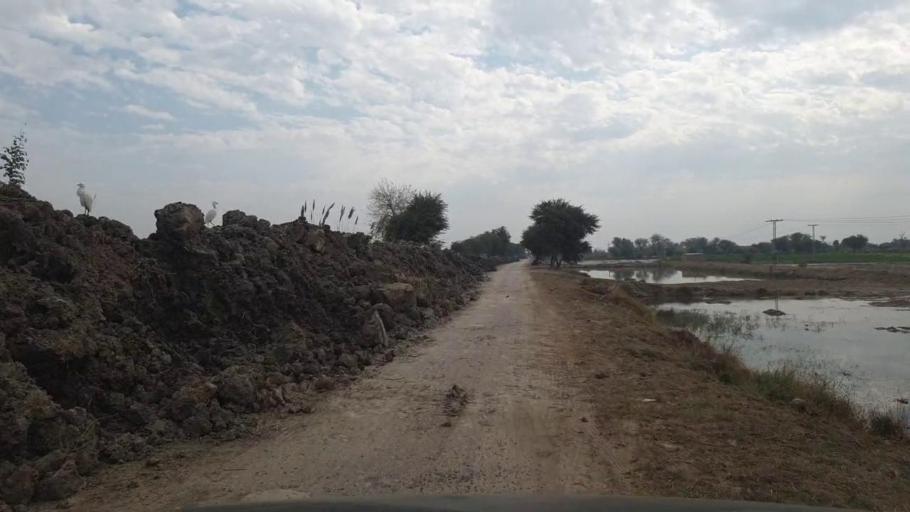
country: PK
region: Sindh
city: Sakrand
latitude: 26.0260
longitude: 68.4269
